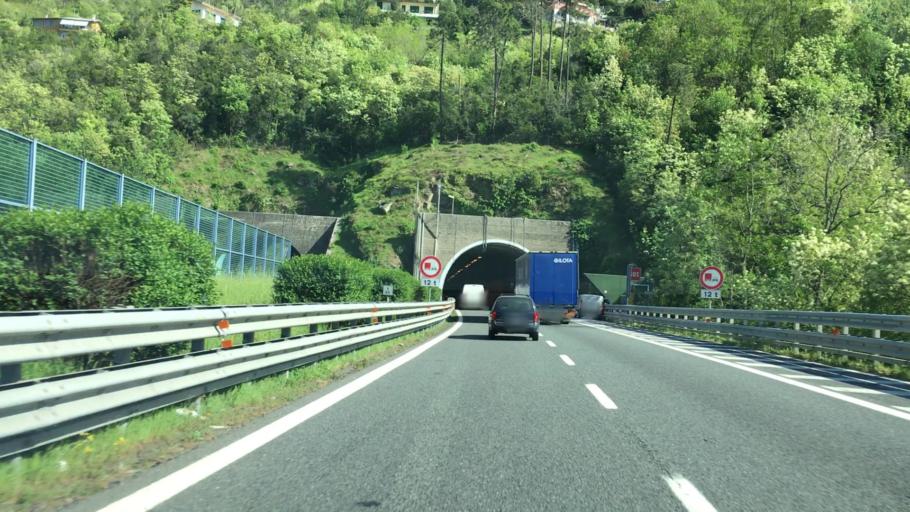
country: IT
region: Liguria
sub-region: Provincia di Genova
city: Sestri Levante
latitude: 44.2920
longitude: 9.3866
